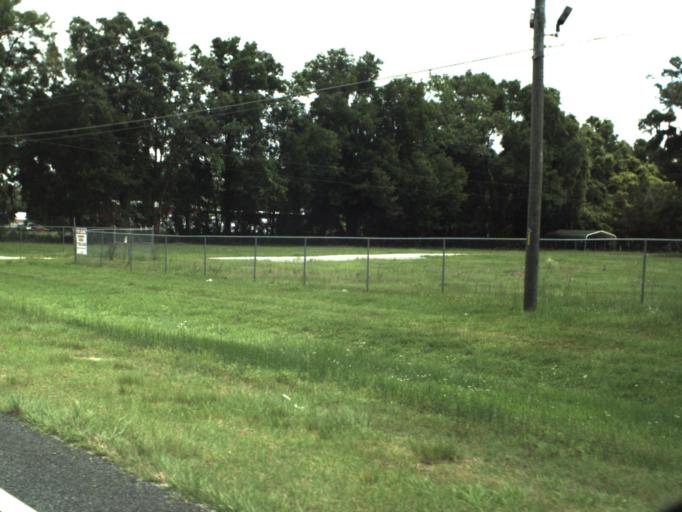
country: US
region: Florida
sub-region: Marion County
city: Ocala
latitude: 29.2650
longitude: -82.1519
